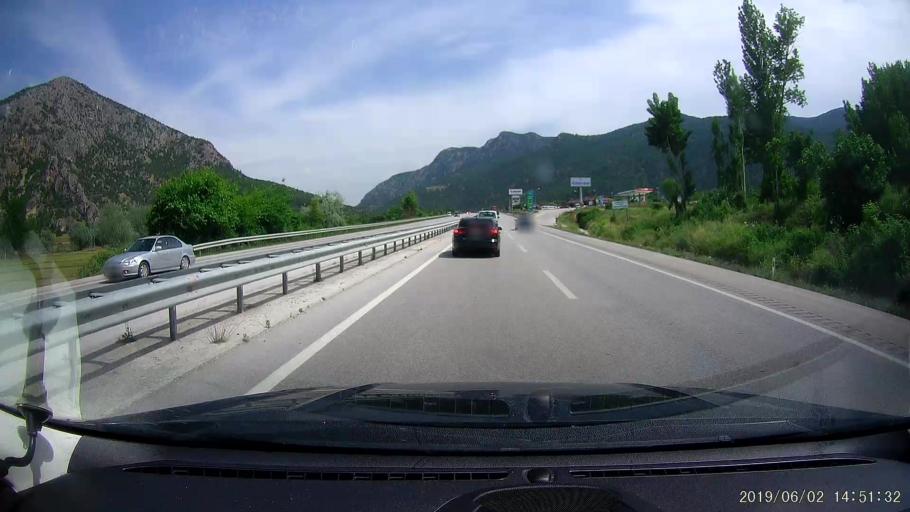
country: TR
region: Corum
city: Kargi
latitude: 41.0583
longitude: 34.5414
